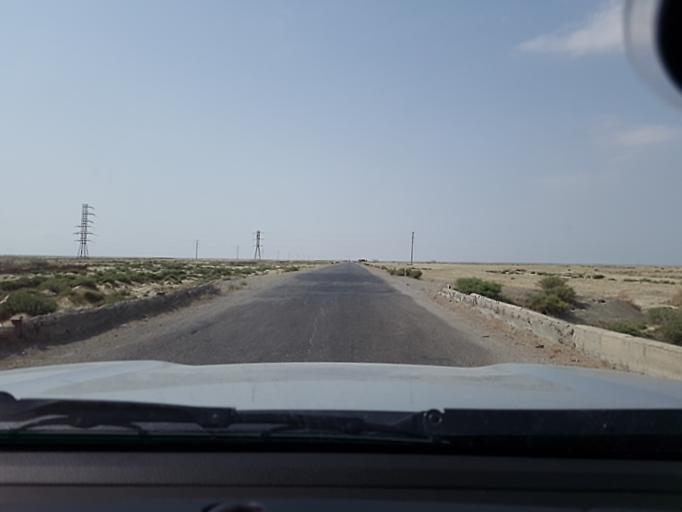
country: TM
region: Balkan
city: Gumdag
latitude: 39.0032
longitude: 54.5860
